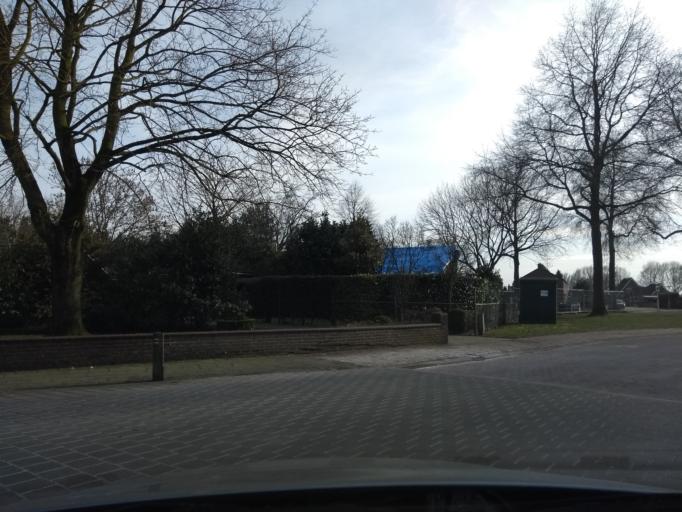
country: NL
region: Overijssel
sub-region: Gemeente Twenterand
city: Vriezenveen
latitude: 52.4230
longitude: 6.6569
